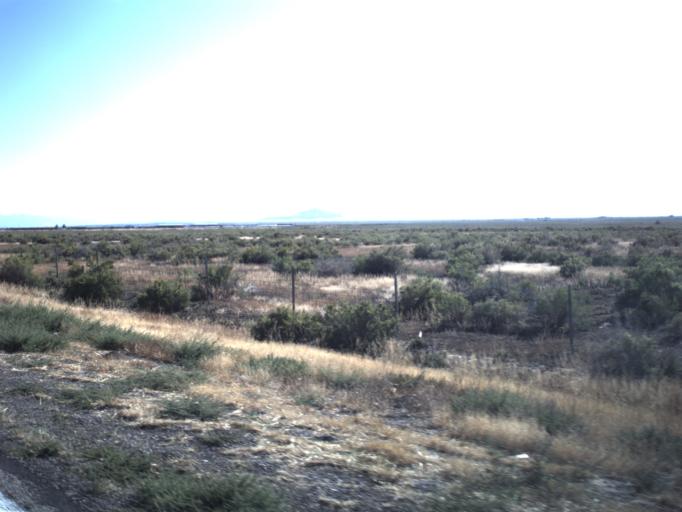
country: US
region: Utah
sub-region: Millard County
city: Delta
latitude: 39.3306
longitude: -112.4871
